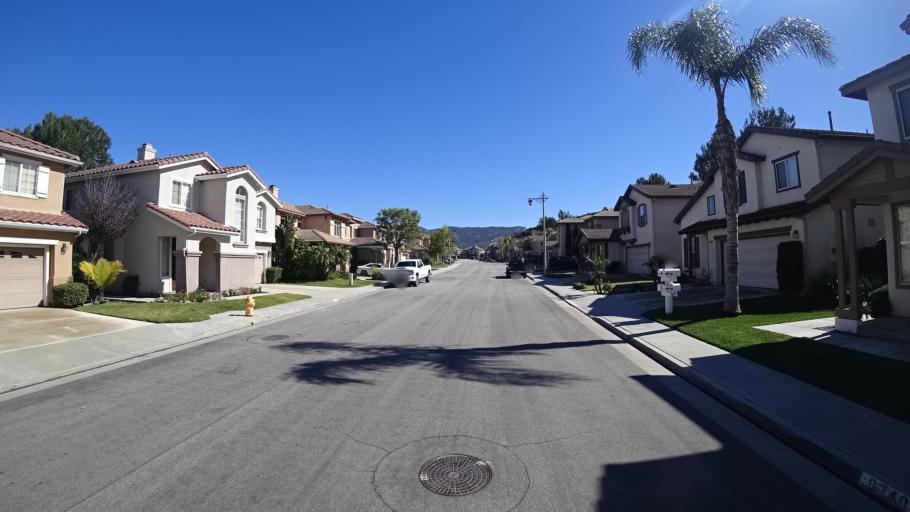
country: US
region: California
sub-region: Orange County
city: Yorba Linda
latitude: 33.8555
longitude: -117.7238
